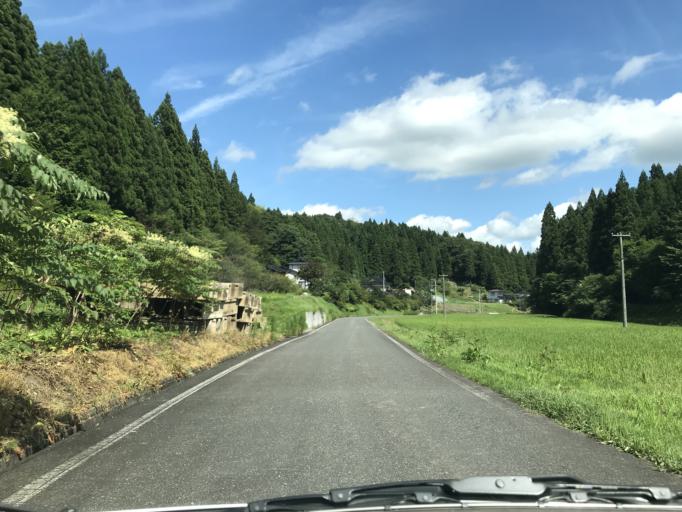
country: JP
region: Iwate
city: Ichinoseki
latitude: 38.9620
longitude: 141.0803
